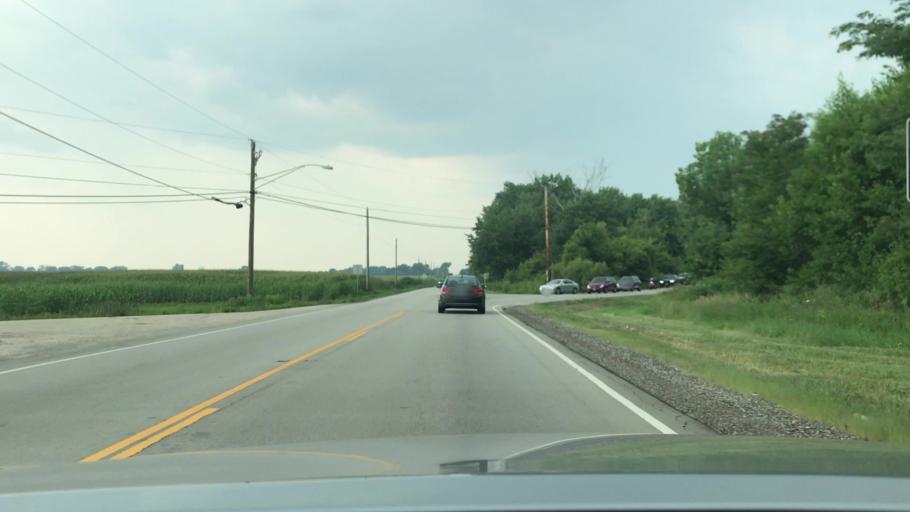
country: US
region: Illinois
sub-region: Will County
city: Plainfield
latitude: 41.6843
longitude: -88.2532
